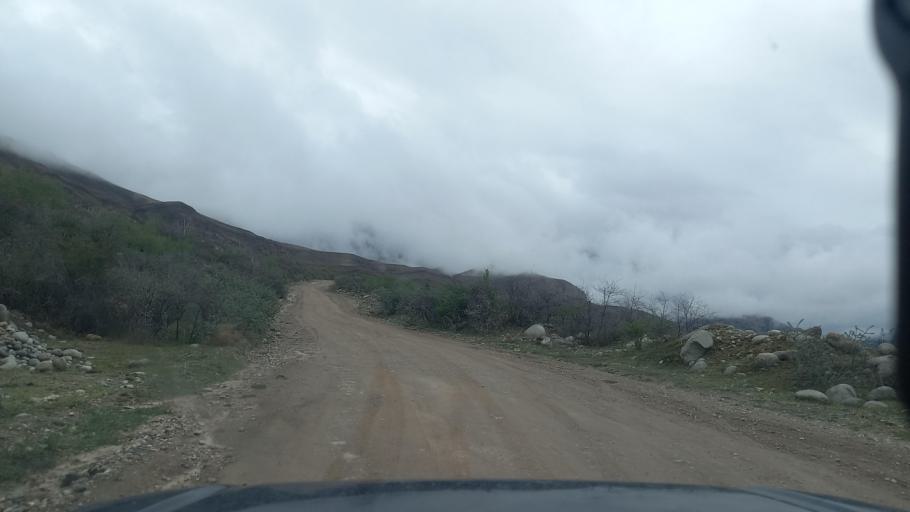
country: RU
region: Kabardino-Balkariya
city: Bylym
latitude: 43.4572
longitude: 43.0082
